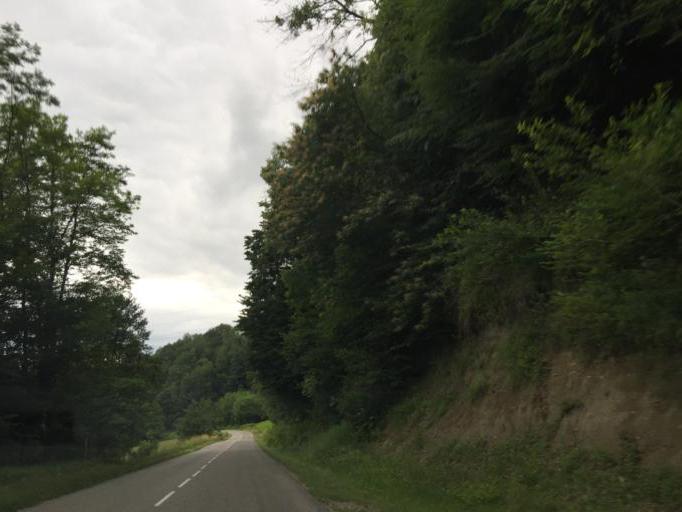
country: FR
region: Rhone-Alpes
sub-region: Departement de la Savoie
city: Le Pont-de-Beauvoisin
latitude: 45.5425
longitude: 5.6815
